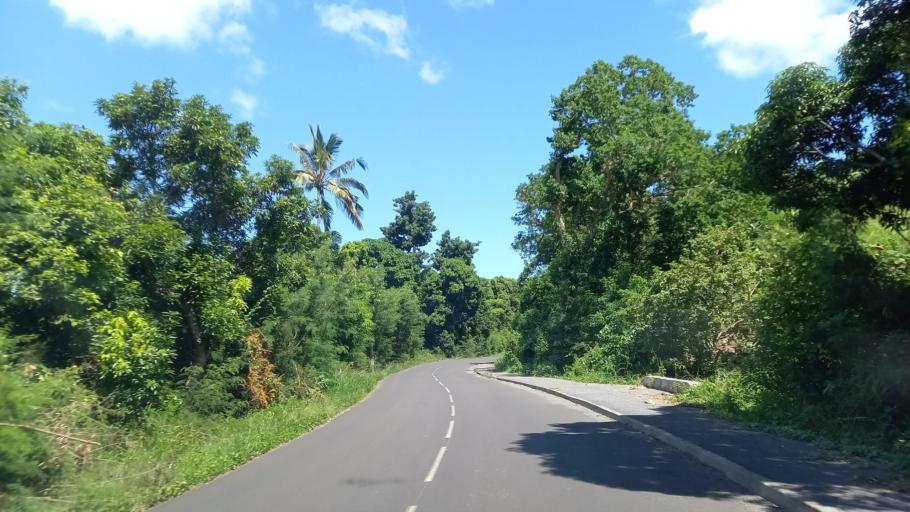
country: YT
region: Boueni
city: Boueni
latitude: -12.9230
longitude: 45.0987
